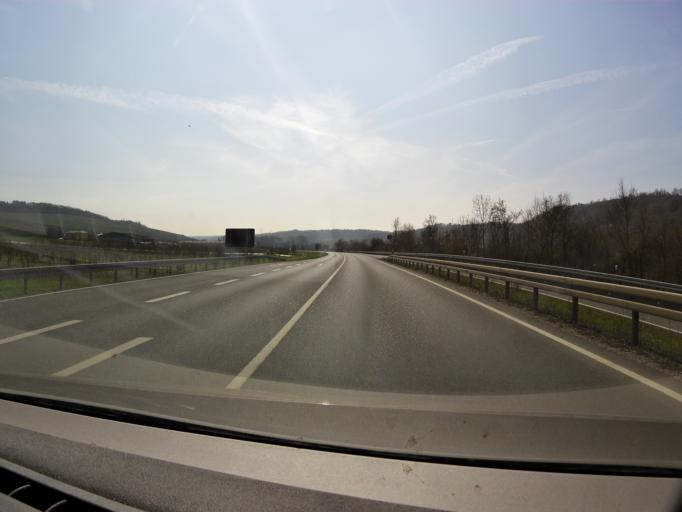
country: DE
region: Bavaria
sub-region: Regierungsbezirk Unterfranken
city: Sommerhausen
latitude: 49.6962
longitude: 10.0237
